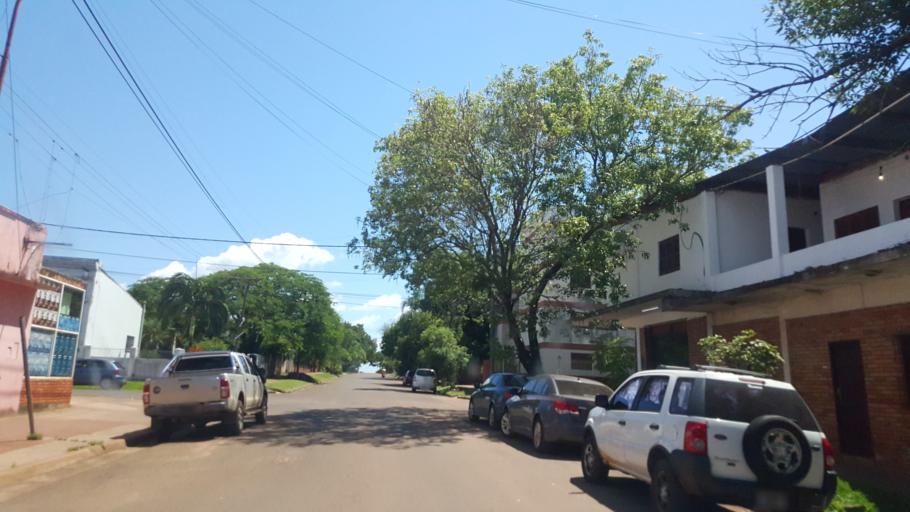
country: AR
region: Corrientes
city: Santo Tome
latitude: -28.5461
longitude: -56.0438
